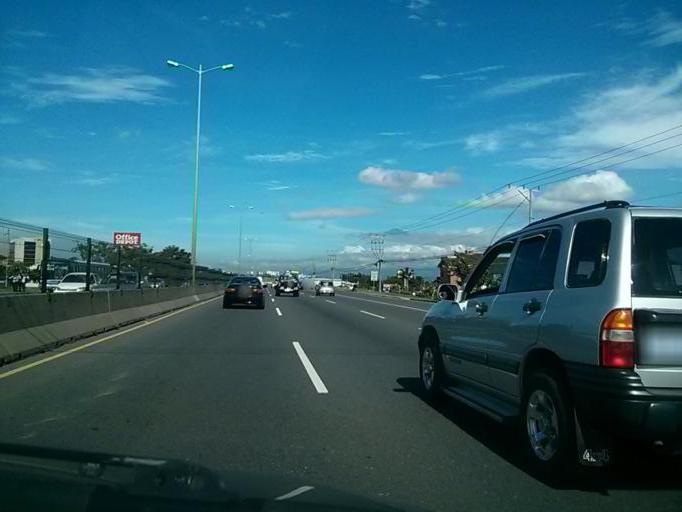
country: CR
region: San Jose
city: San Rafael
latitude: 9.9415
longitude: -84.1449
